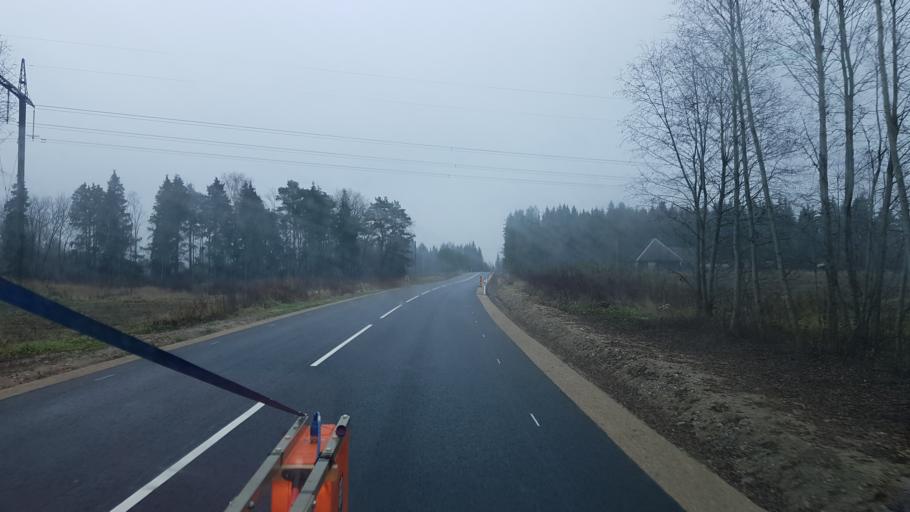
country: EE
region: Raplamaa
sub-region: Kohila vald
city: Kohila
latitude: 59.1778
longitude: 24.8159
